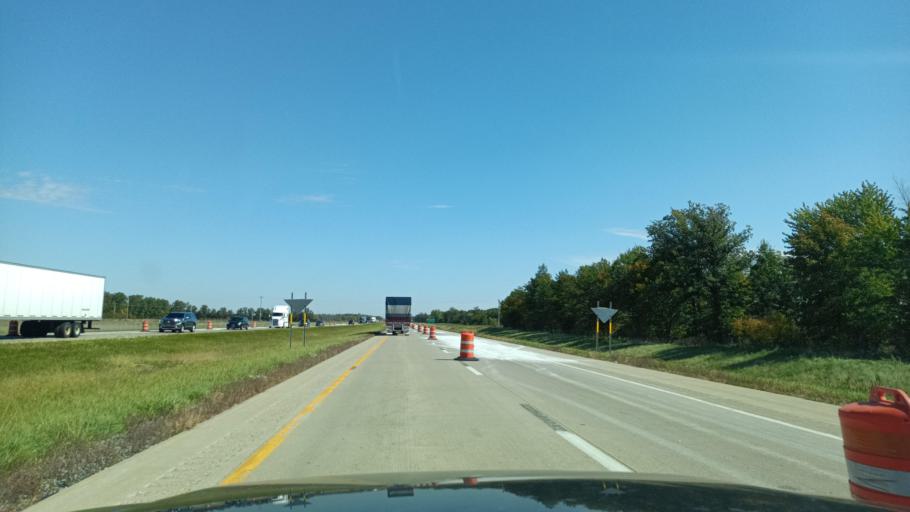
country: US
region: Ohio
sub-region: Paulding County
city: Paulding
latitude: 41.2352
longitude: -84.5376
